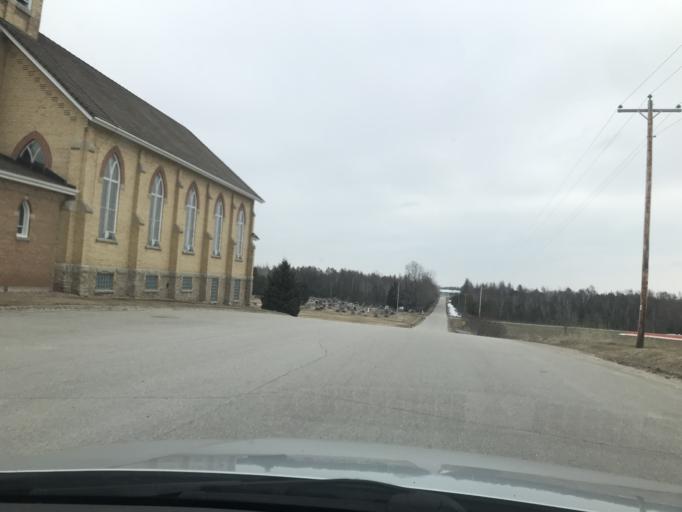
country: US
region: Wisconsin
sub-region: Marinette County
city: Peshtigo
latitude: 45.0273
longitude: -87.8707
